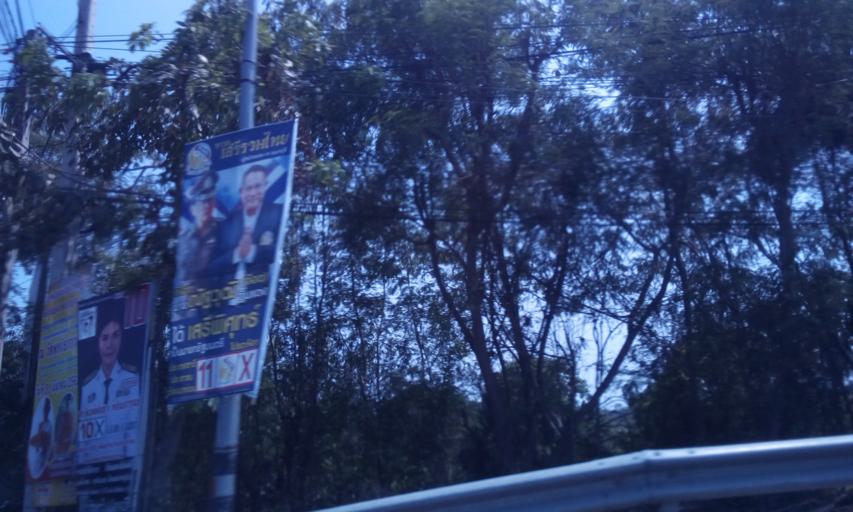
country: TH
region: Nonthaburi
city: Bang Yai
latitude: 13.9097
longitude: 100.3576
